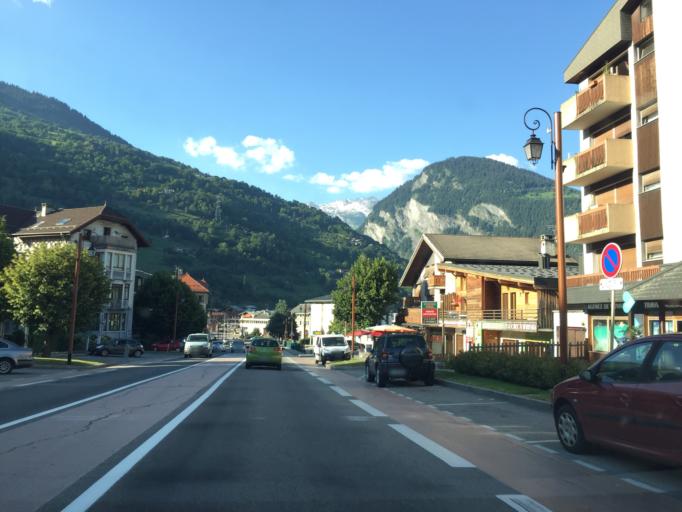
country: FR
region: Rhone-Alpes
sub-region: Departement de la Savoie
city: Bourg-Saint-Maurice
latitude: 45.6167
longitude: 6.7703
